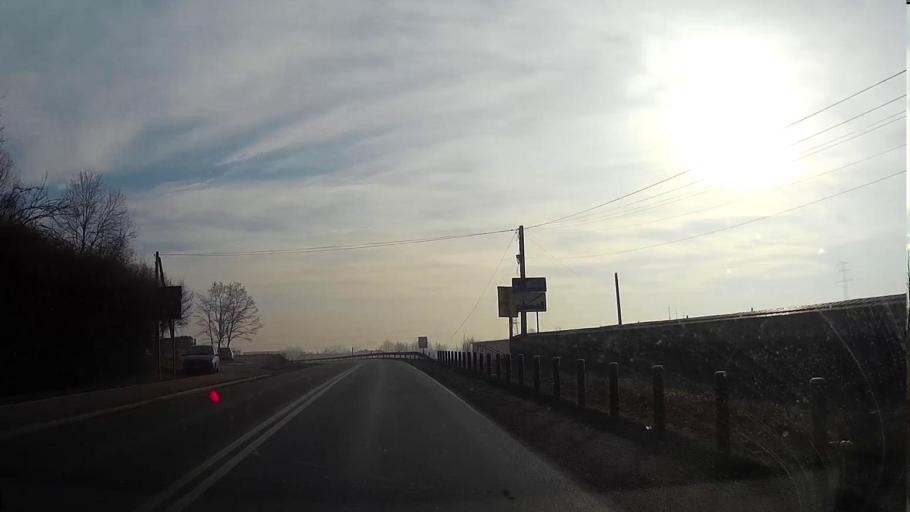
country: PL
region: Lesser Poland Voivodeship
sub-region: Powiat krakowski
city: Kryspinow
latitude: 50.0413
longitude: 19.7997
